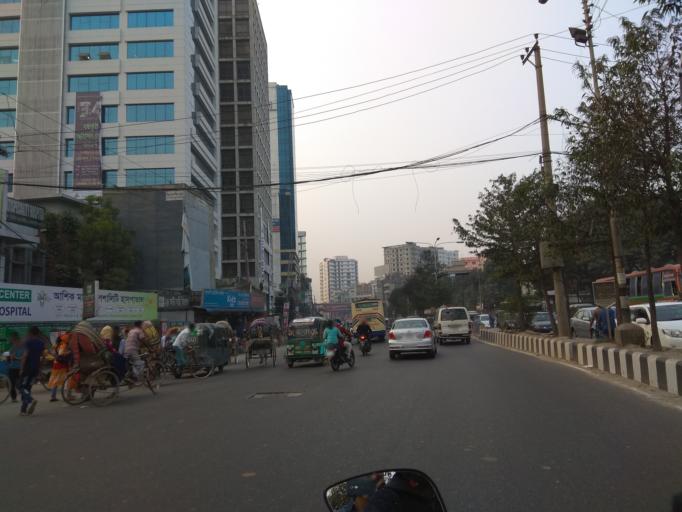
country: BD
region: Dhaka
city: Azimpur
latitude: 23.7729
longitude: 90.3673
